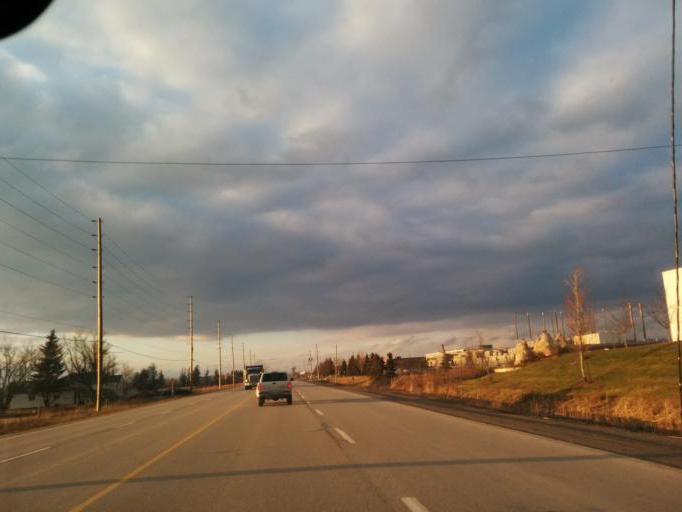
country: CA
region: Ontario
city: Brampton
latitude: 43.8500
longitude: -79.7210
